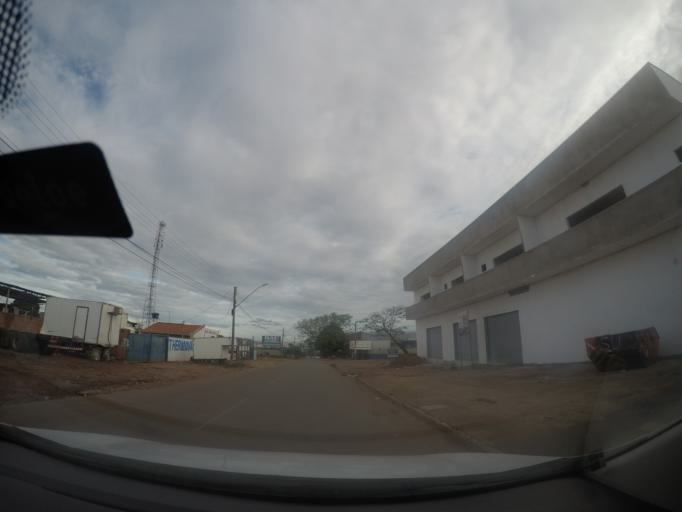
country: BR
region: Goias
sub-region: Goiania
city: Goiania
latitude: -16.6533
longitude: -49.3195
